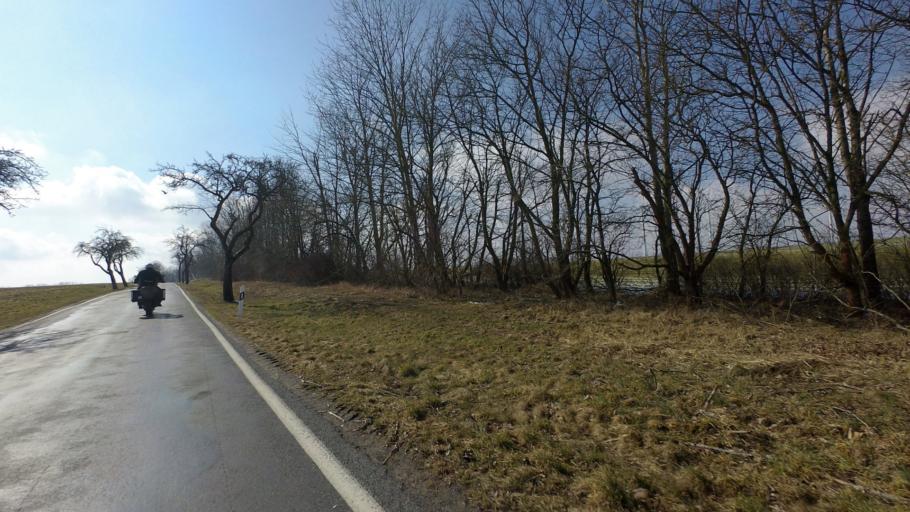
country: DE
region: Brandenburg
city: Werneuchen
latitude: 52.7024
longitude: 13.7199
